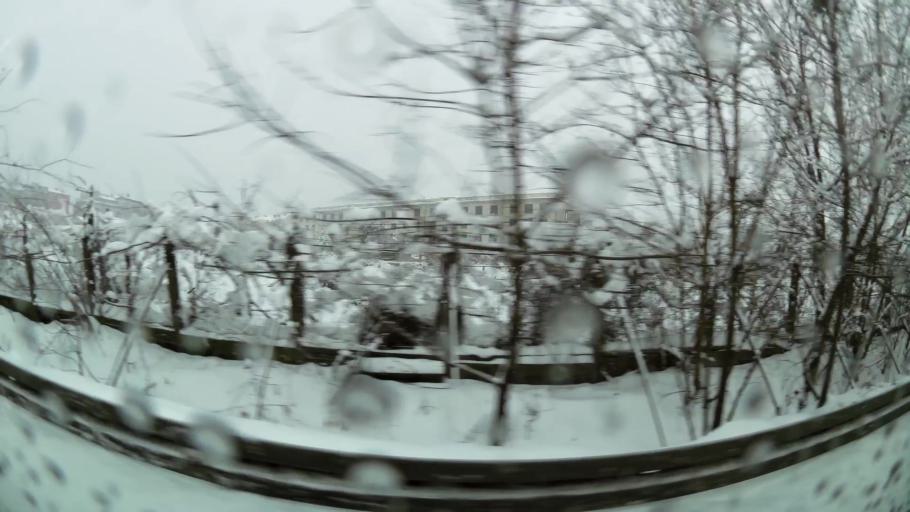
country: RS
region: Central Serbia
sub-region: Belgrade
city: Stari Grad
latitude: 44.8287
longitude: 20.4538
